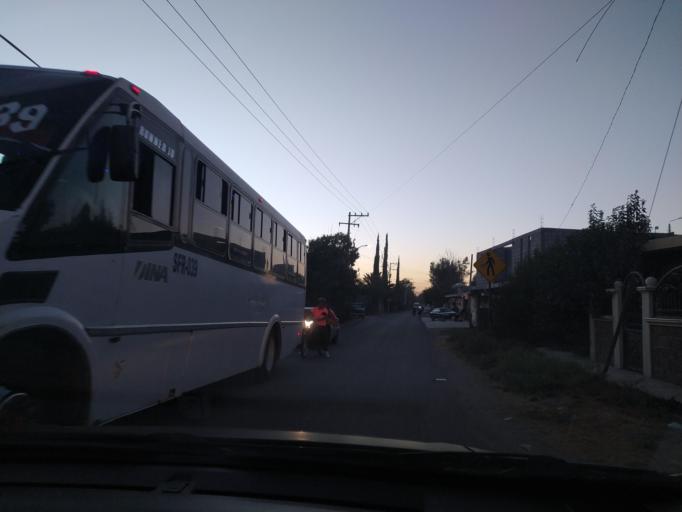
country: LA
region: Oudomxai
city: Muang La
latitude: 21.0098
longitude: 101.8112
